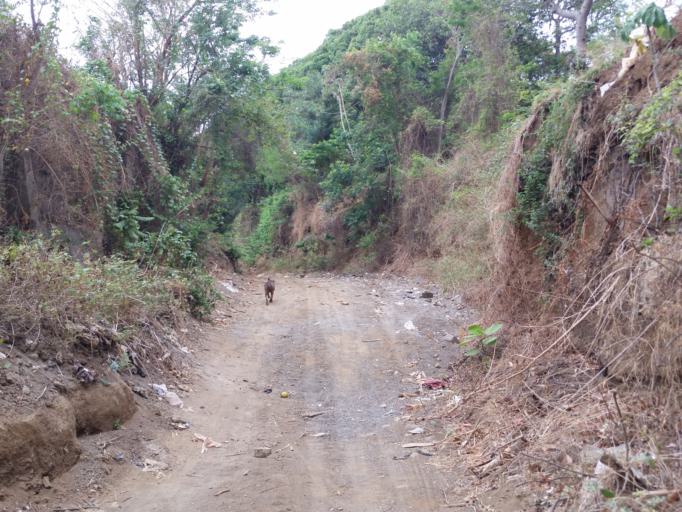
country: NI
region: Managua
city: Managua
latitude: 12.0683
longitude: -86.2535
